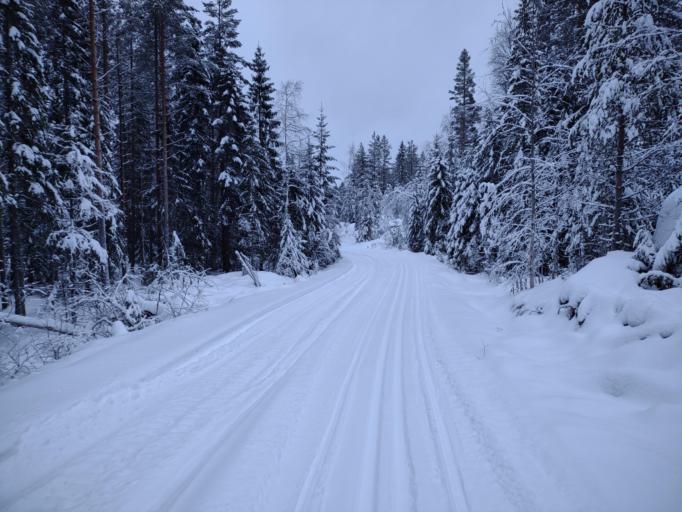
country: NO
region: Buskerud
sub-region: Flesberg
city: Lampeland
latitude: 59.7238
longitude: 9.5402
